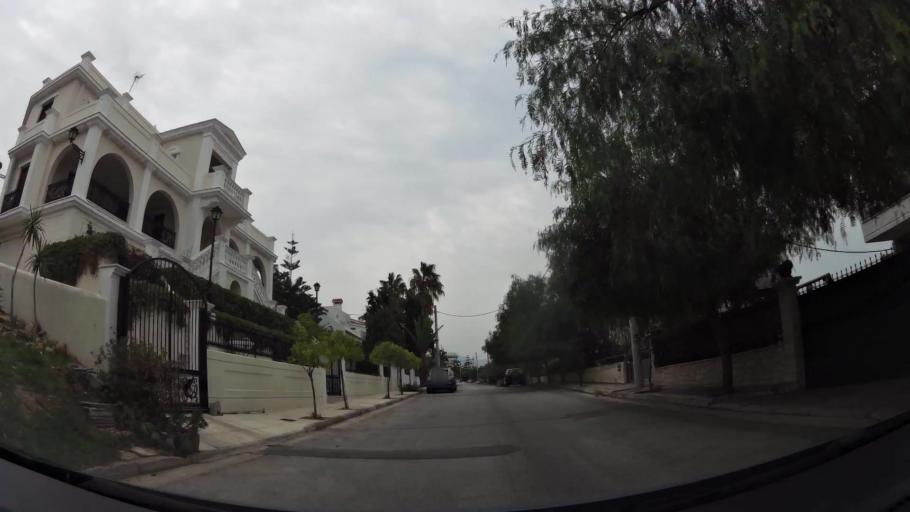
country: GR
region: Attica
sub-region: Nomarchia Athinas
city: Alimos
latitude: 37.9097
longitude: 23.7270
